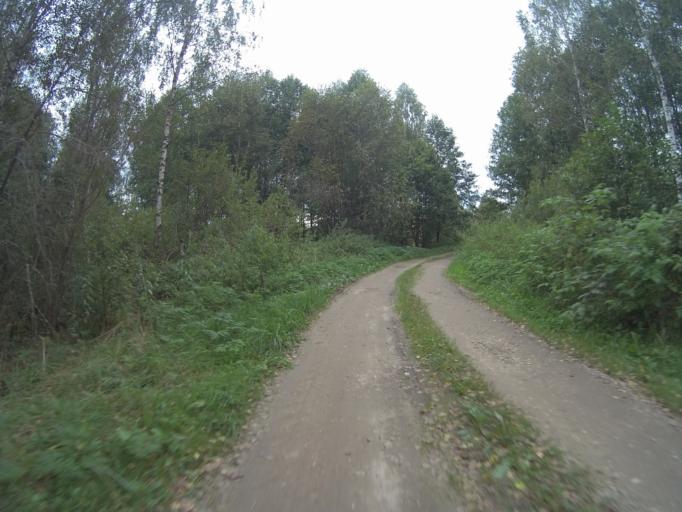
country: RU
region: Vladimir
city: Golovino
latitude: 55.9738
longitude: 40.4628
